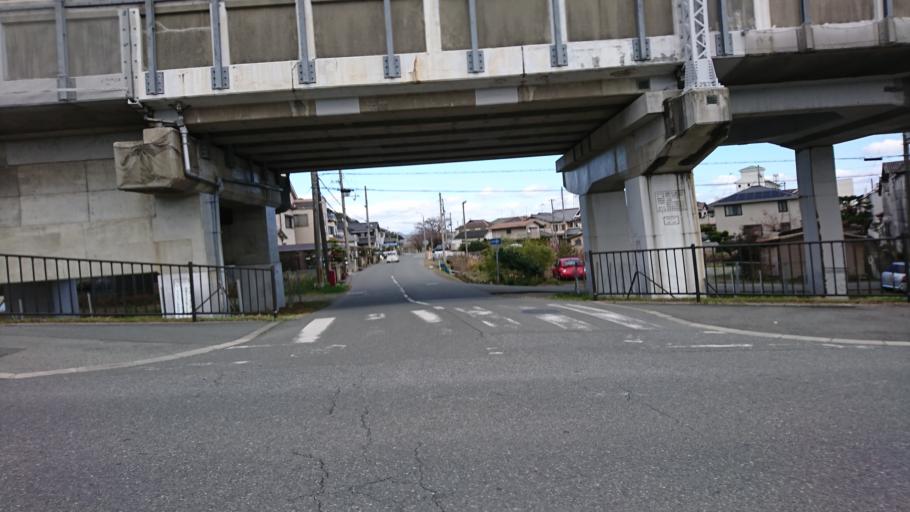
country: JP
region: Hyogo
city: Kakogawacho-honmachi
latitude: 34.7705
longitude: 134.7943
